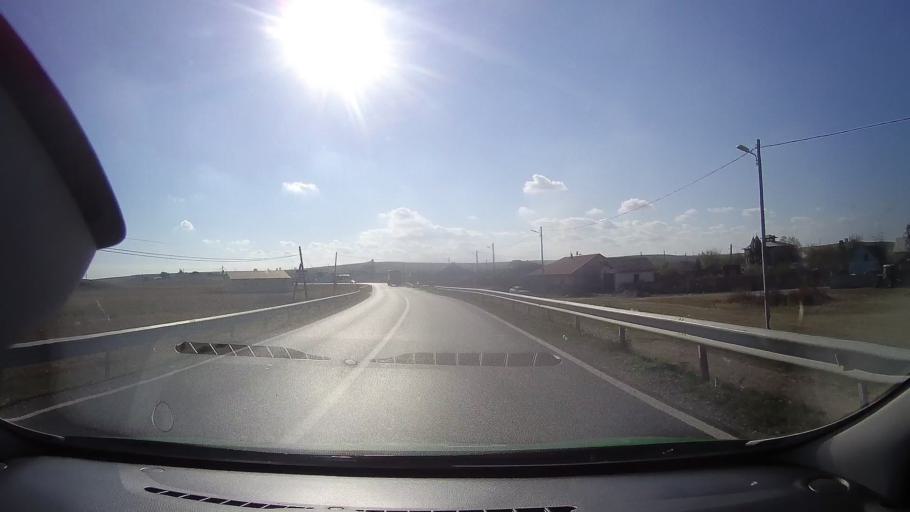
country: RO
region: Tulcea
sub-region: Comuna Baia
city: Baia
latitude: 44.7228
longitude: 28.6795
